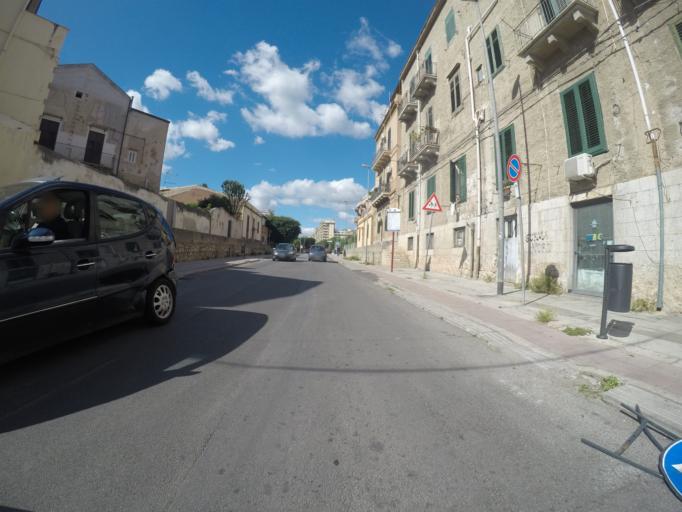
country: IT
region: Sicily
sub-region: Palermo
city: Palermo
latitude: 38.1444
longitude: 13.3671
